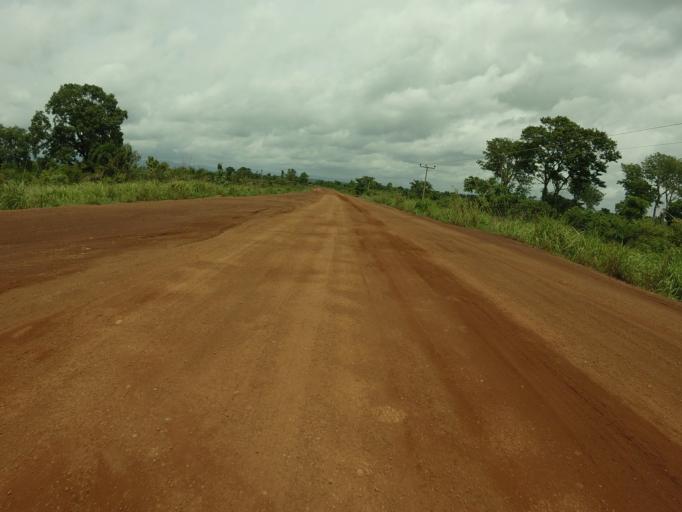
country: GH
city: Kpandae
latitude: 8.4071
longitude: 0.3971
